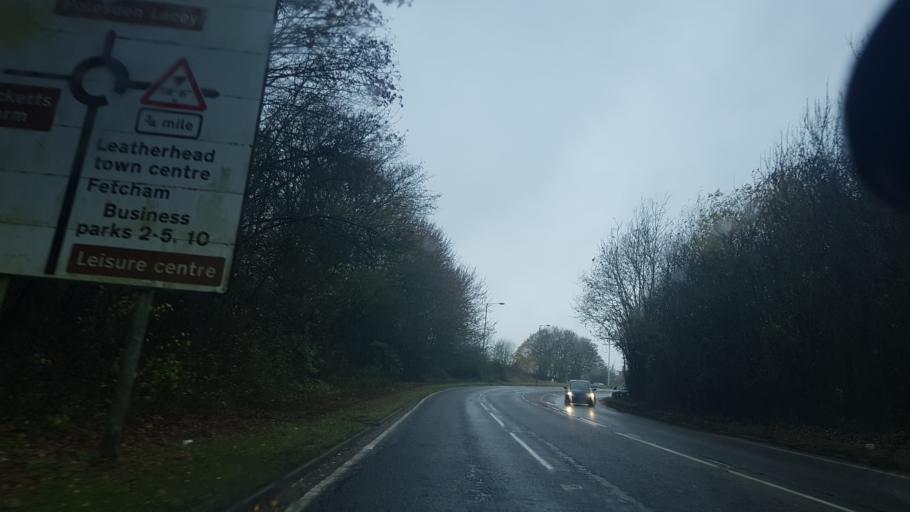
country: GB
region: England
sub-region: Surrey
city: Leatherhead
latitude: 51.2822
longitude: -0.3478
